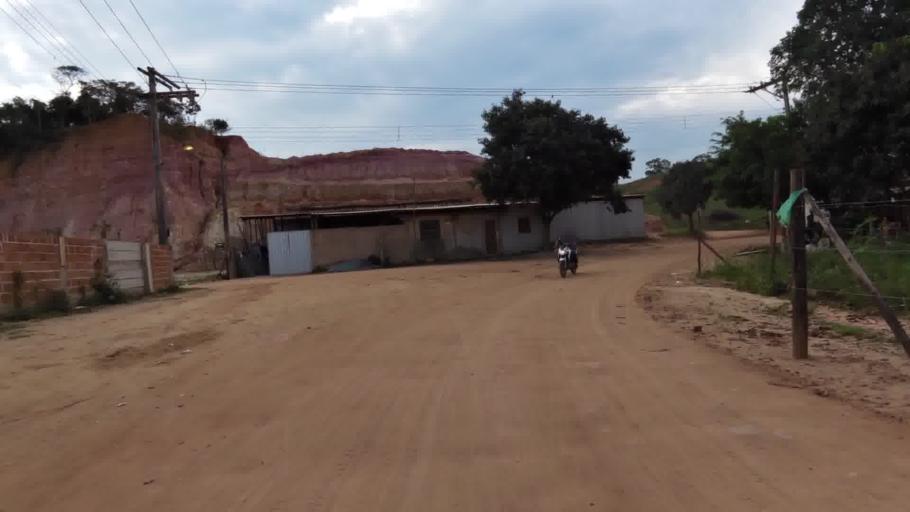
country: BR
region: Espirito Santo
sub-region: Piuma
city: Piuma
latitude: -20.8380
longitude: -40.7454
